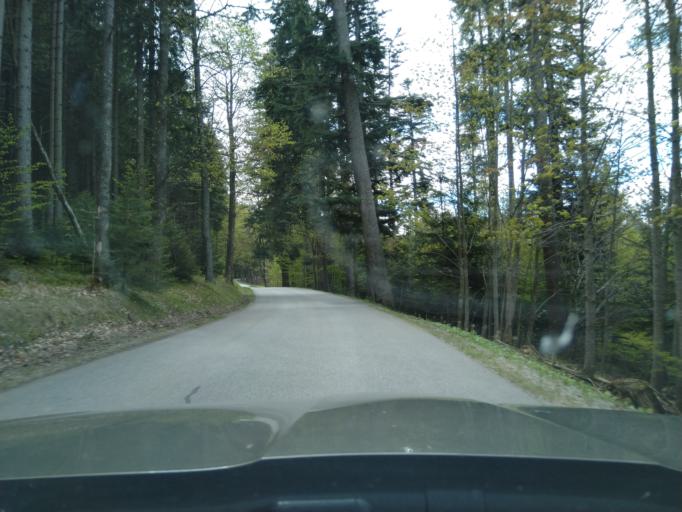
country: CZ
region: Jihocesky
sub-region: Okres Prachatice
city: Borova Lada
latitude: 49.0111
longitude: 13.7130
